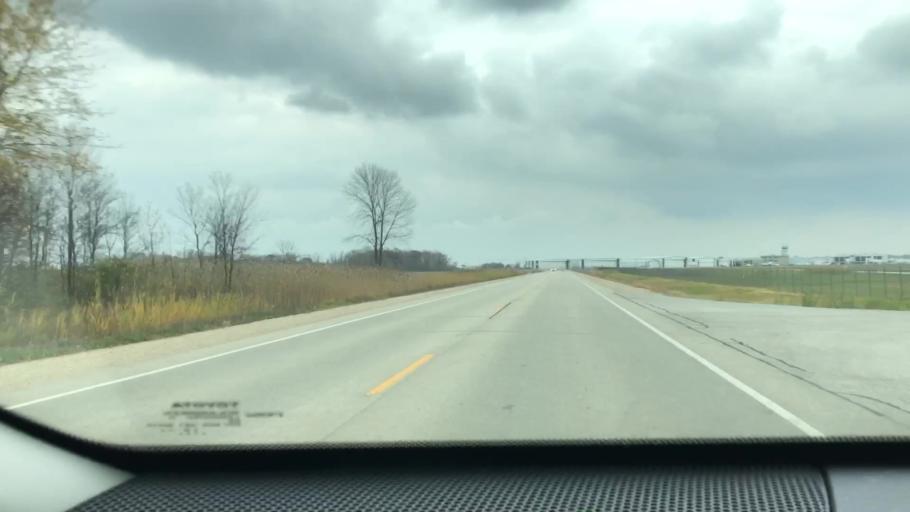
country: US
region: Wisconsin
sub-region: Brown County
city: Oneida
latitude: 44.4977
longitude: -88.1394
